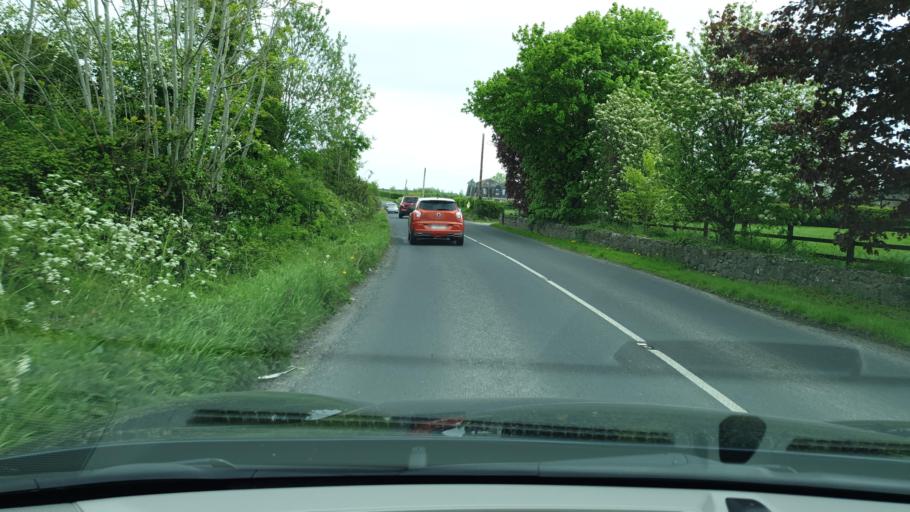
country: IE
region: Leinster
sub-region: An Mhi
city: Ashbourne
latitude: 53.5104
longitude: -6.4277
